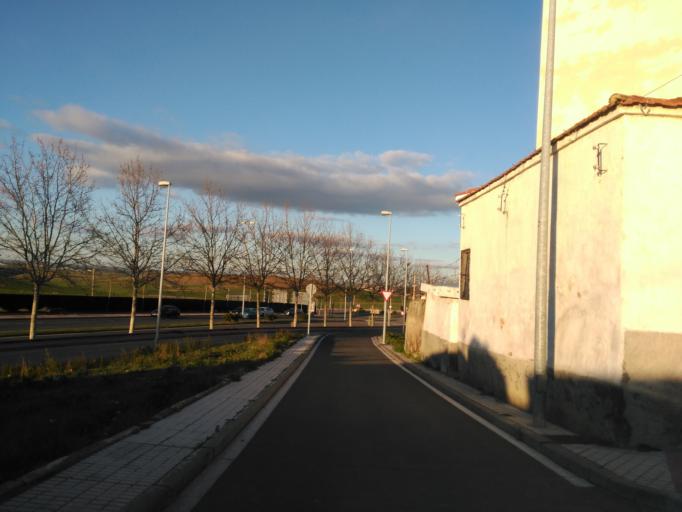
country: ES
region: Castille and Leon
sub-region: Provincia de Salamanca
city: Salamanca
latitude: 40.9800
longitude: -5.6785
